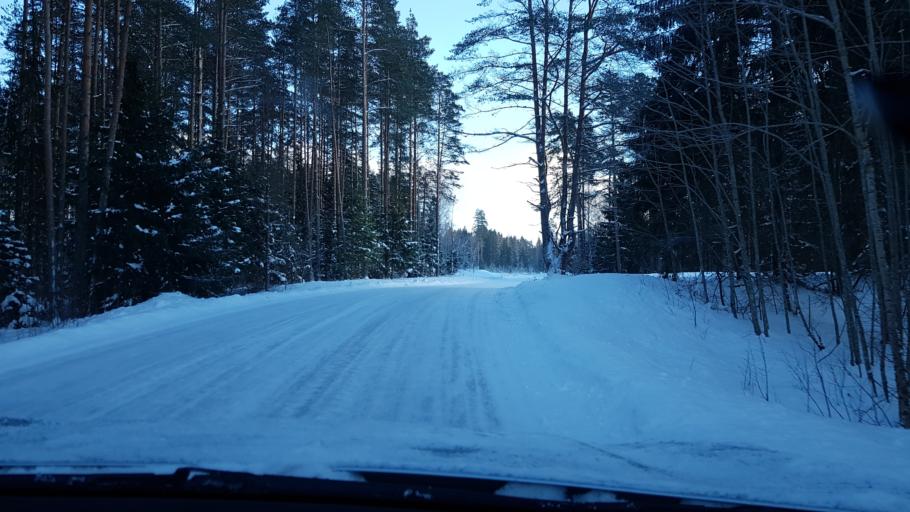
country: EE
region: Harju
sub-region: Nissi vald
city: Turba
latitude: 59.1377
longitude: 24.1811
